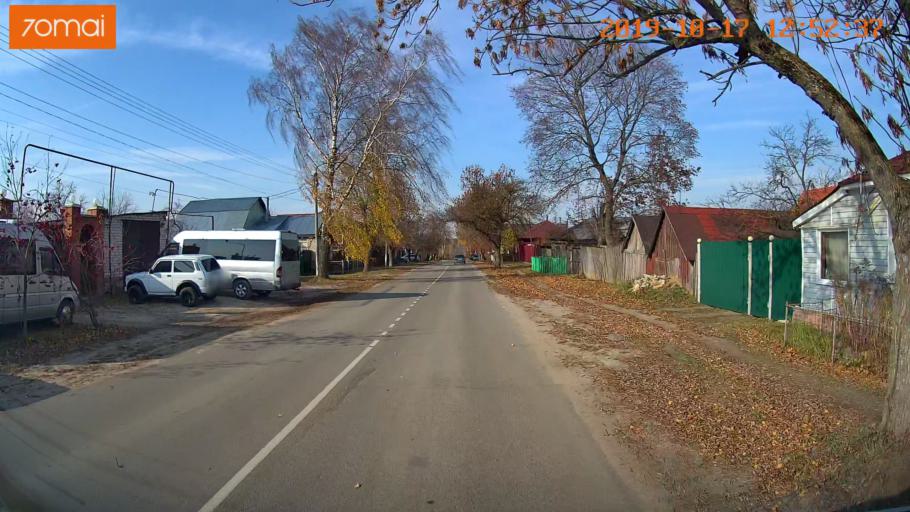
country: RU
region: Rjazan
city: Kasimov
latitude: 54.9431
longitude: 41.3884
